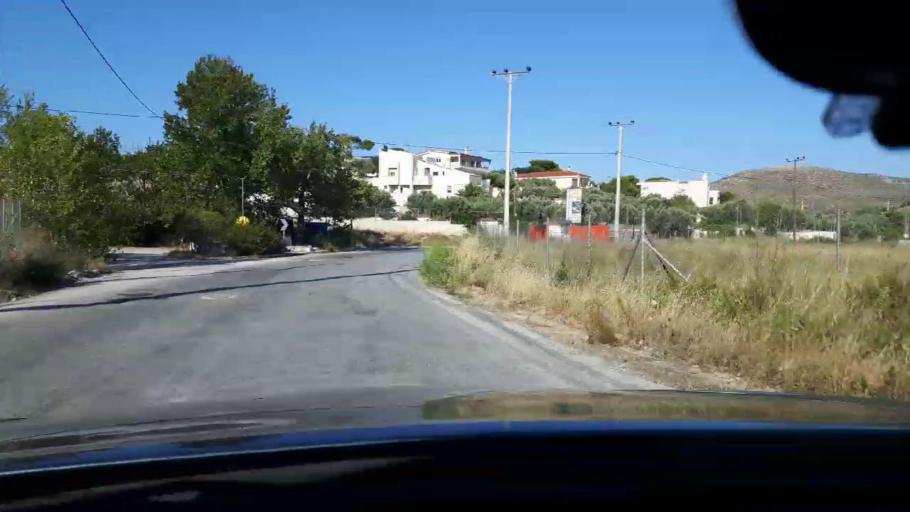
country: GR
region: Attica
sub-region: Nomarchia Anatolikis Attikis
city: Markopoulo
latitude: 37.8865
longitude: 23.9620
